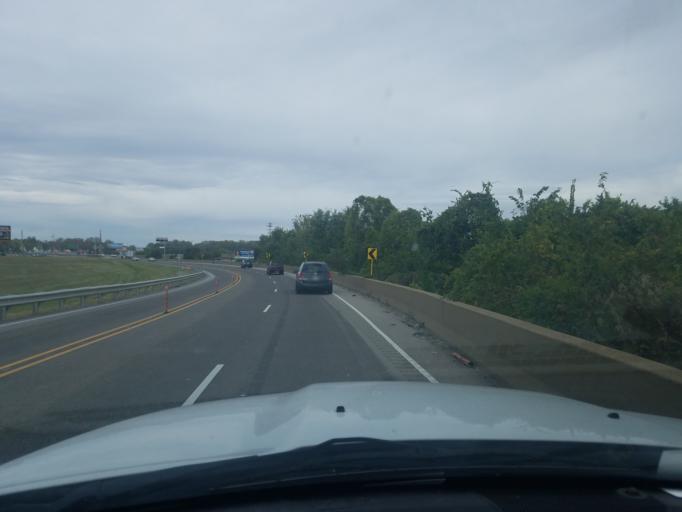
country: US
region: Indiana
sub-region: Vanderburgh County
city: Evansville
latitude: 37.9117
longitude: -87.5479
